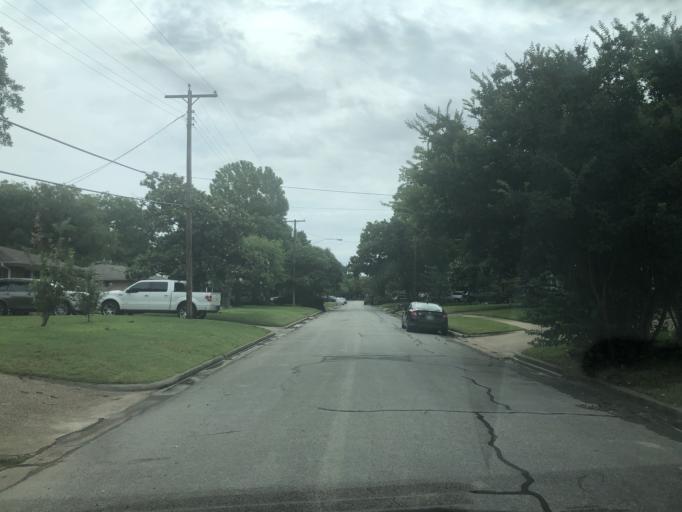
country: US
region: Texas
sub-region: Dallas County
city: Irving
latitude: 32.8074
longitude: -96.9464
